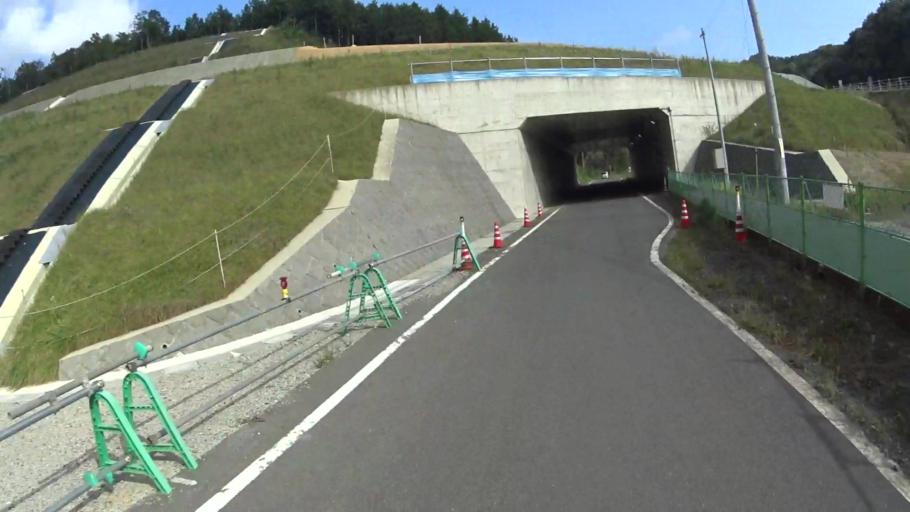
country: JP
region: Kyoto
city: Miyazu
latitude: 35.5675
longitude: 135.1201
